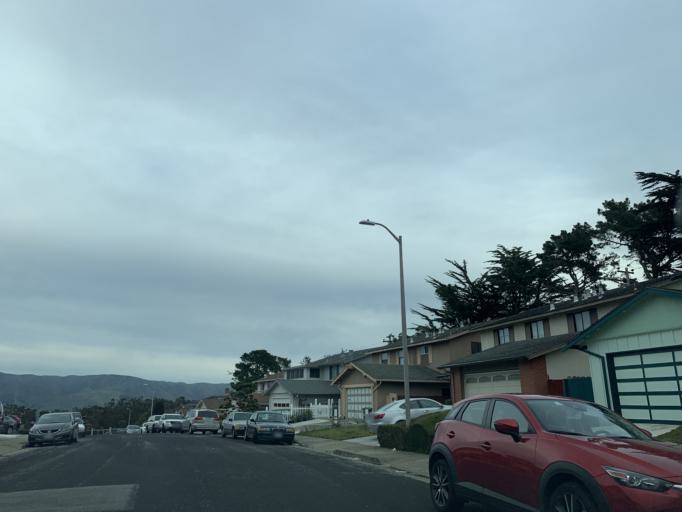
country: US
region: California
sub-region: San Mateo County
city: Colma
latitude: 37.6403
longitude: -122.4496
